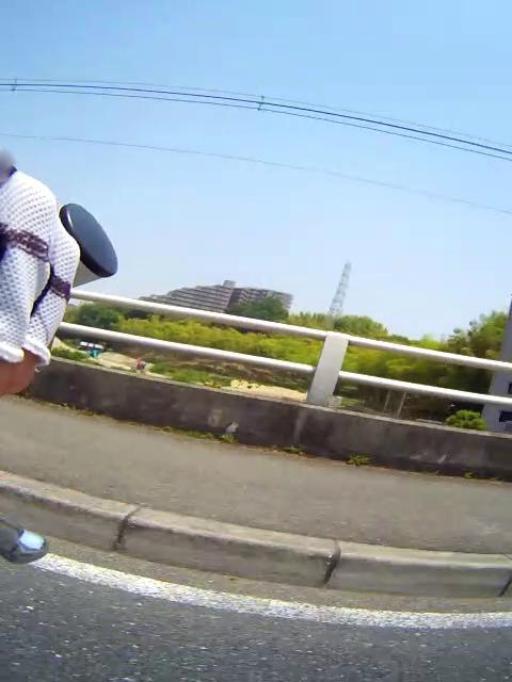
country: JP
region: Osaka
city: Suita
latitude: 34.7825
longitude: 135.4973
